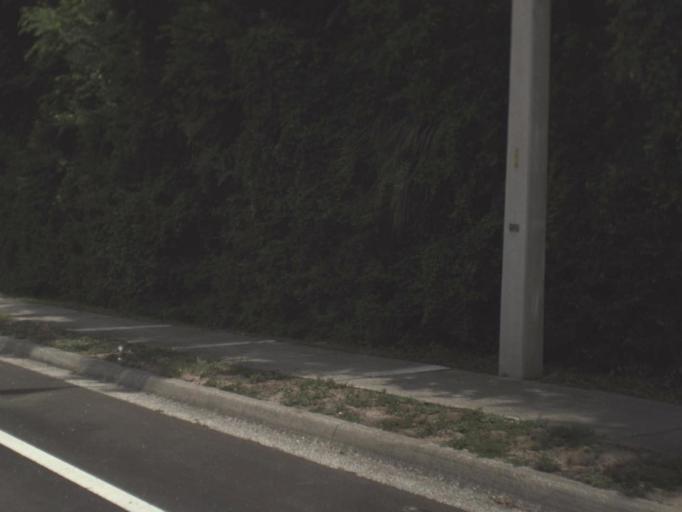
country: US
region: Florida
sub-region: Alachua County
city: Gainesville
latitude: 29.6407
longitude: -82.2843
